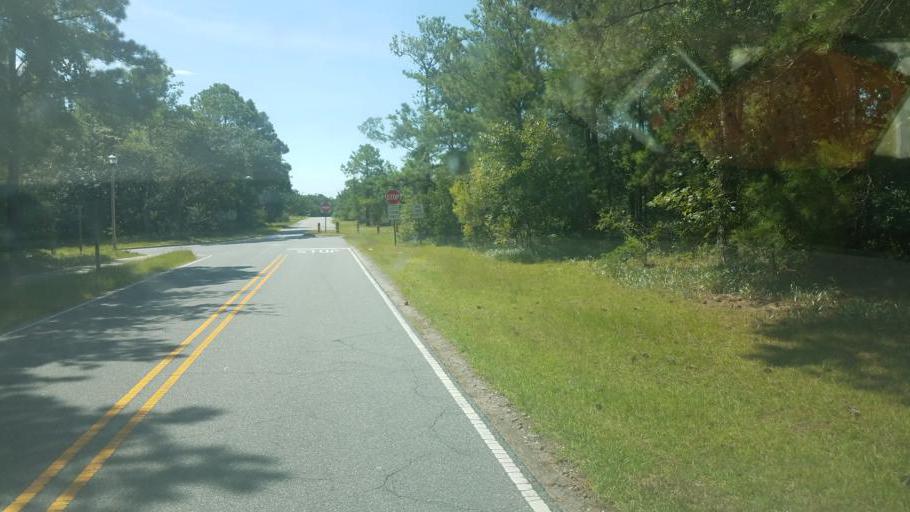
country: US
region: North Carolina
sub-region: Dare County
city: Kill Devil Hills
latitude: 36.0058
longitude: -75.6625
